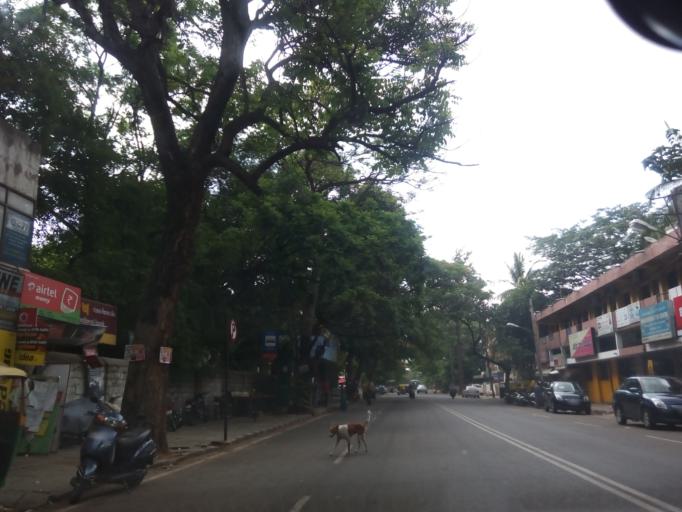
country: IN
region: Karnataka
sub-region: Bangalore Urban
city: Bangalore
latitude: 13.0090
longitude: 77.5631
